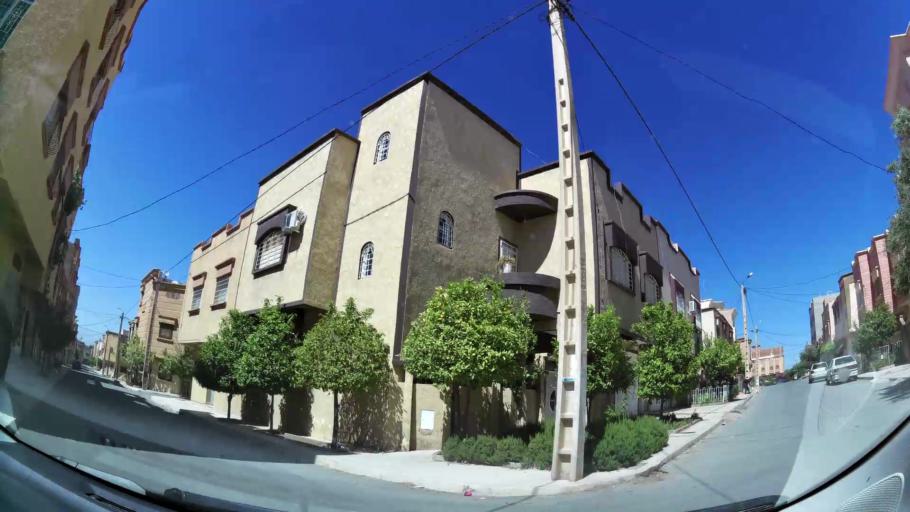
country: MA
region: Oriental
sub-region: Oujda-Angad
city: Oujda
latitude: 34.6626
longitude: -1.8769
